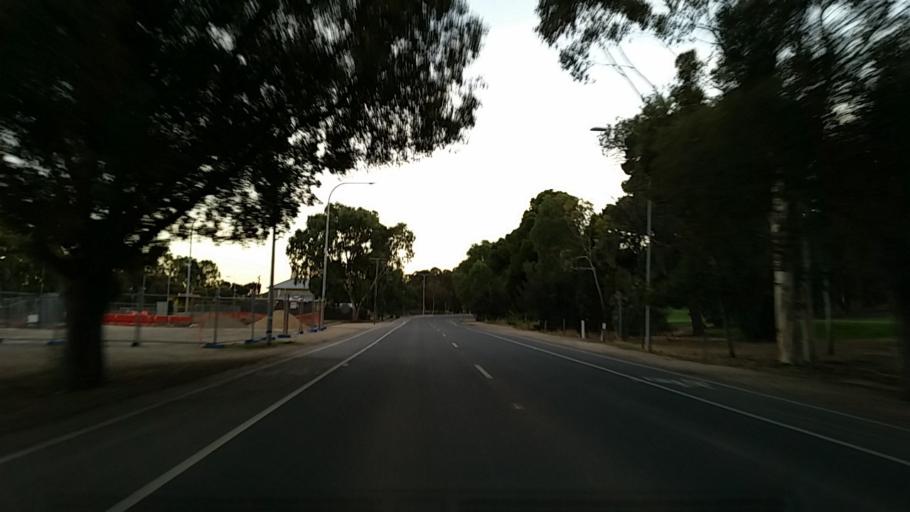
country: AU
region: South Australia
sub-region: Adelaide
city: North Adelaide
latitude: -34.9075
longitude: 138.5817
